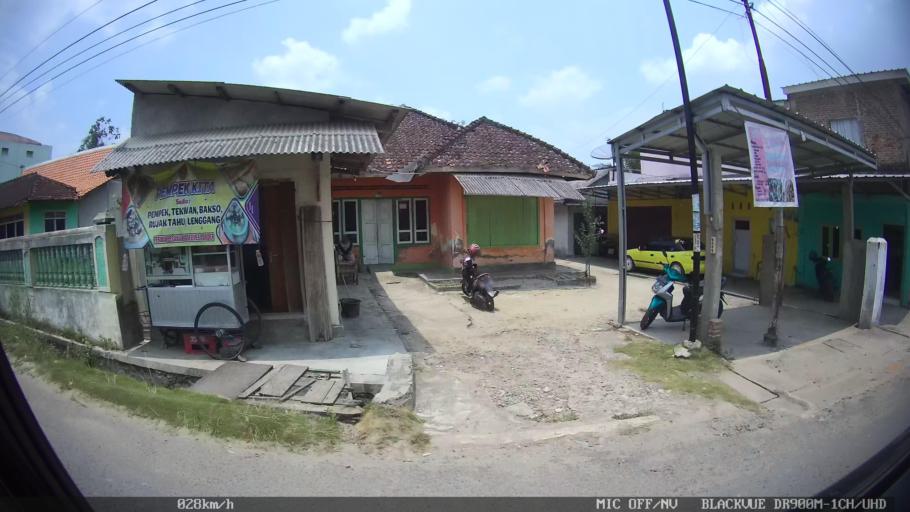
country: ID
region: Lampung
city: Pringsewu
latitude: -5.3521
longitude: 104.9691
